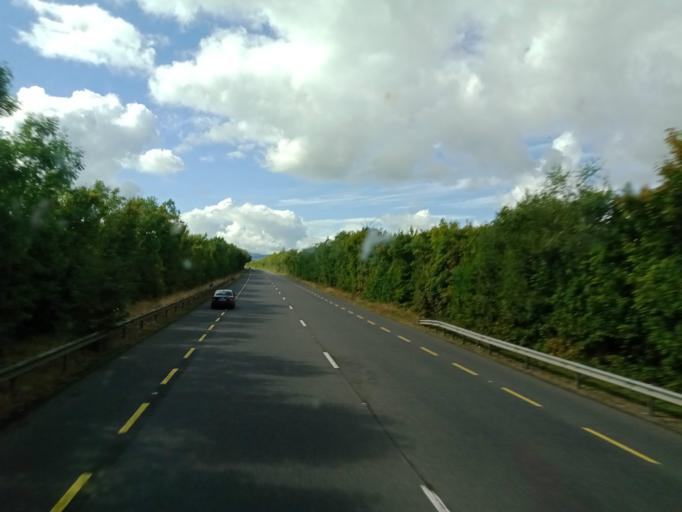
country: IE
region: Munster
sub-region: Waterford
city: Portlaw
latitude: 52.1953
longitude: -7.4339
